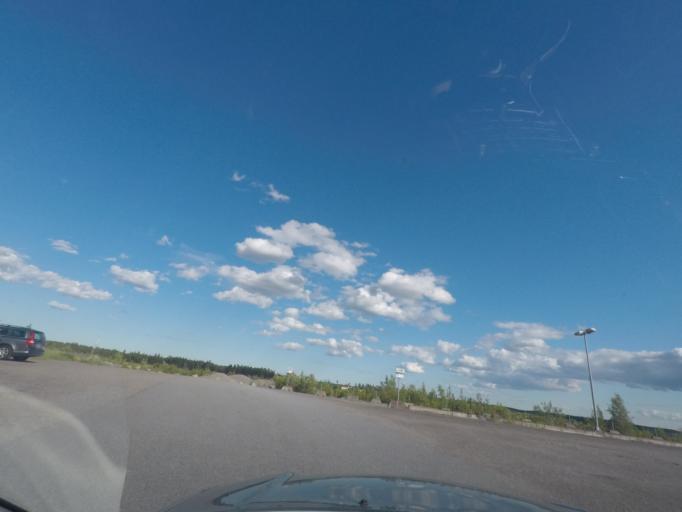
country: SE
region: Stockholm
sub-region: Sigtuna Kommun
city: Rosersberg
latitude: 59.6545
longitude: 17.9568
